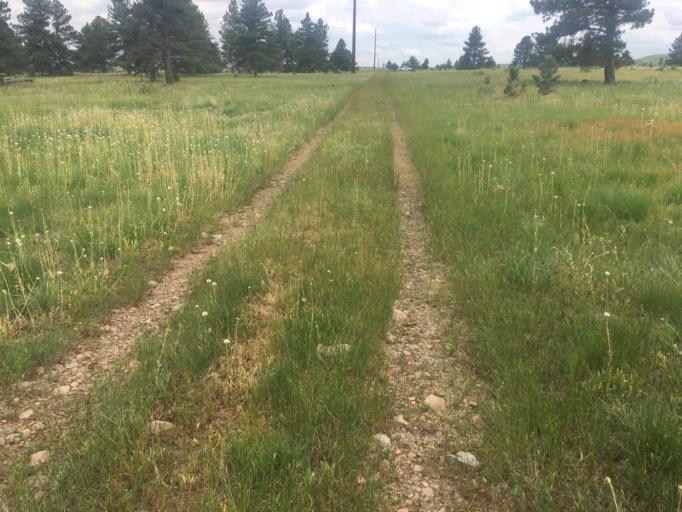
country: US
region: Colorado
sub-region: Boulder County
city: Superior
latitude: 39.9168
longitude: -105.2522
